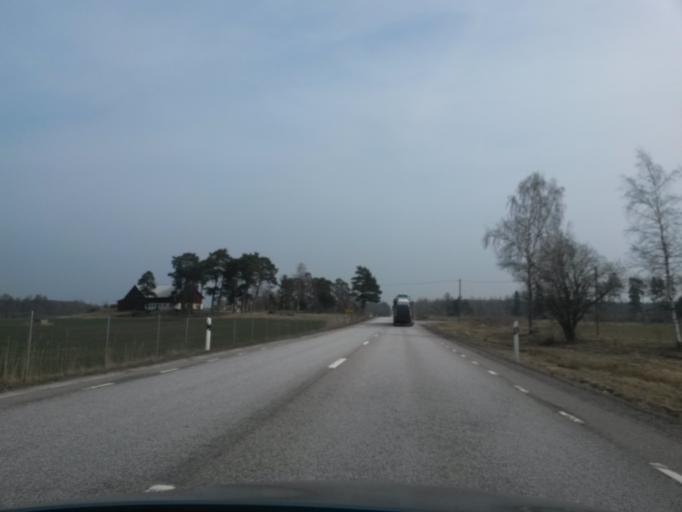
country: SE
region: Vaestra Goetaland
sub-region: Gullspangs Kommun
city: Anderstorp
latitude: 58.8686
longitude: 14.2386
